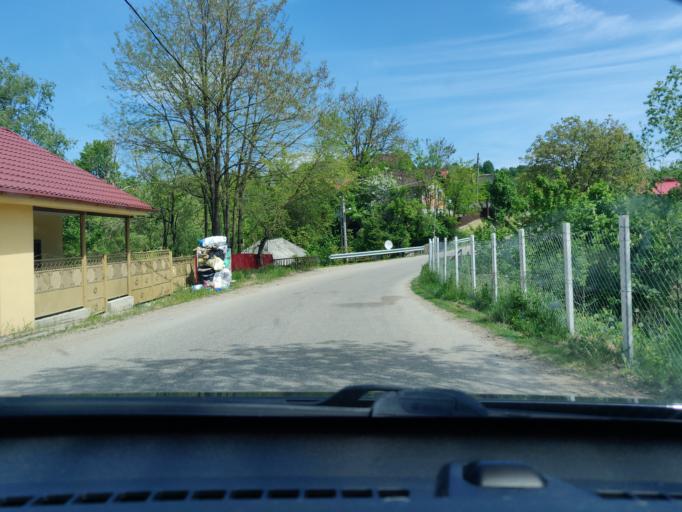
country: RO
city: Vizantea-Manastireasca
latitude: 45.9891
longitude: 26.7748
